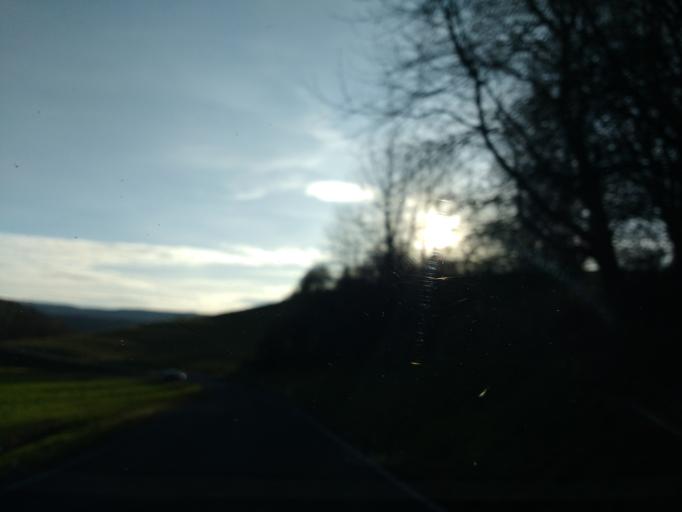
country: DE
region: Thuringia
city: Burgwalde
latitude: 51.3849
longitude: 10.0410
